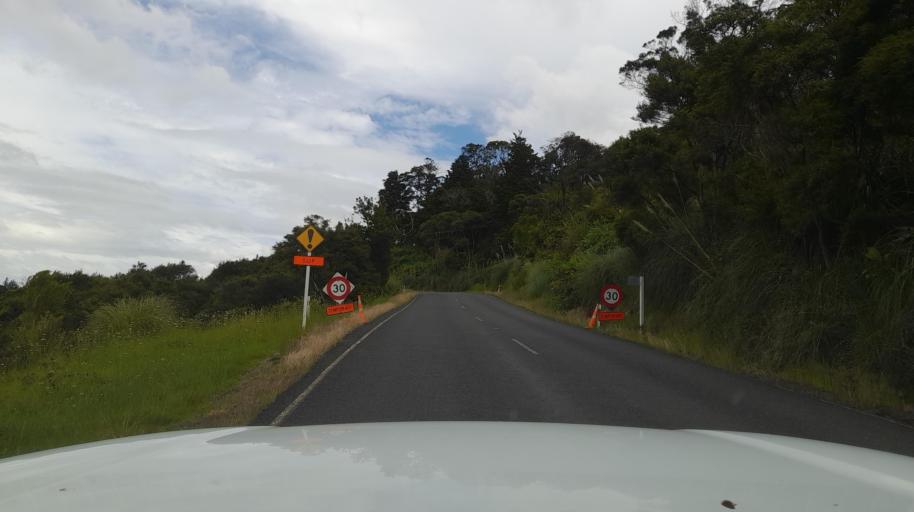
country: NZ
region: Northland
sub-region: Far North District
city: Kaitaia
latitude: -35.3731
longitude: 173.3800
